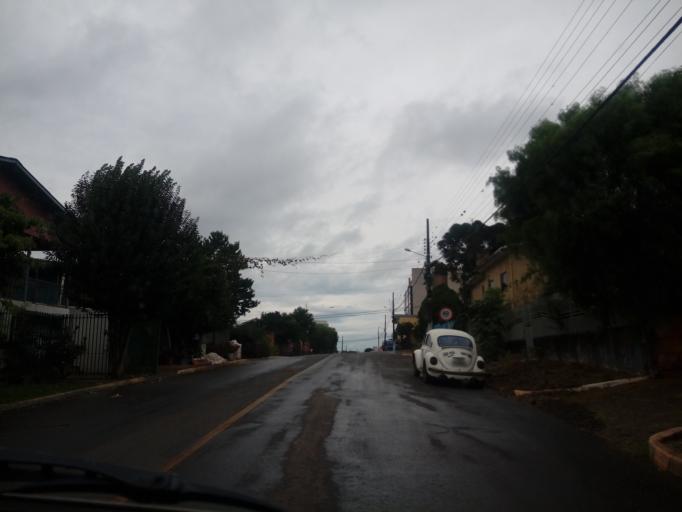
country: BR
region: Santa Catarina
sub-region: Chapeco
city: Chapeco
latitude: -27.0972
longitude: -52.6784
